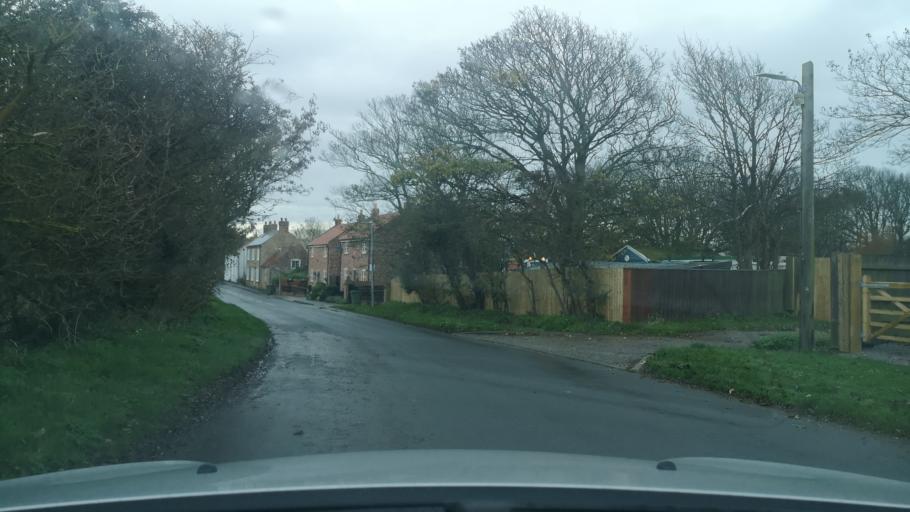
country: GB
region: England
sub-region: East Riding of Yorkshire
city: Easington
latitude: 53.6501
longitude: 0.1201
